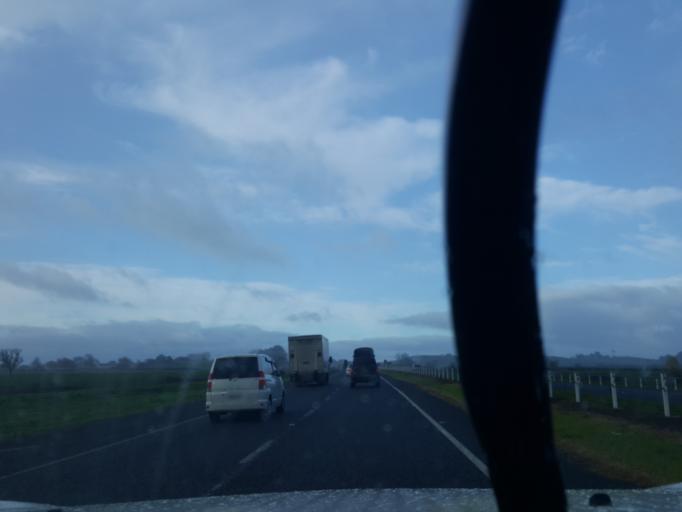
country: NZ
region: Waikato
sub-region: Waikato District
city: Ngaruawahia
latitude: -37.6570
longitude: 175.2058
